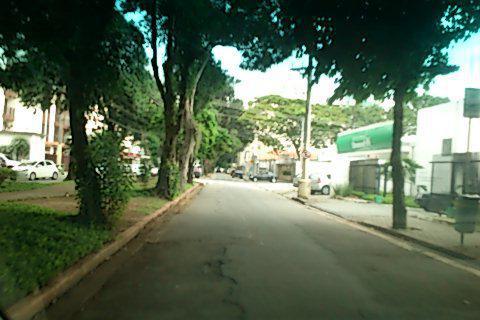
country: BR
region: Sao Paulo
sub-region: Sao Jose Dos Campos
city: Sao Jose dos Campos
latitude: -23.2080
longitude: -45.8903
